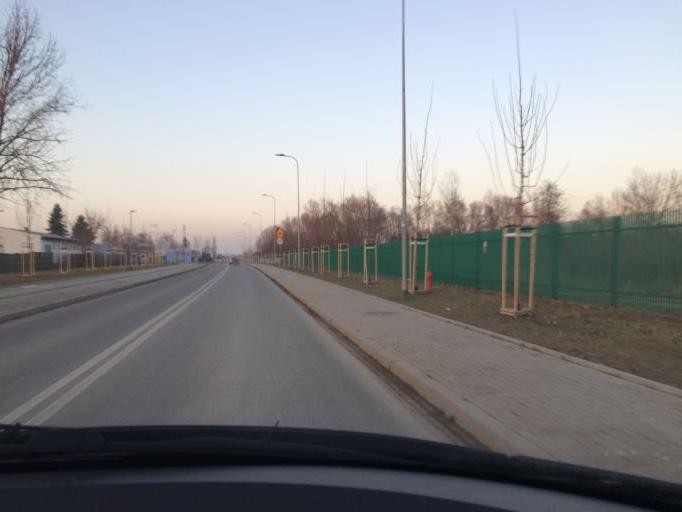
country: PL
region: Lesser Poland Voivodeship
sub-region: Powiat wielicki
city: Czarnochowice
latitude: 50.0269
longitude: 20.0516
